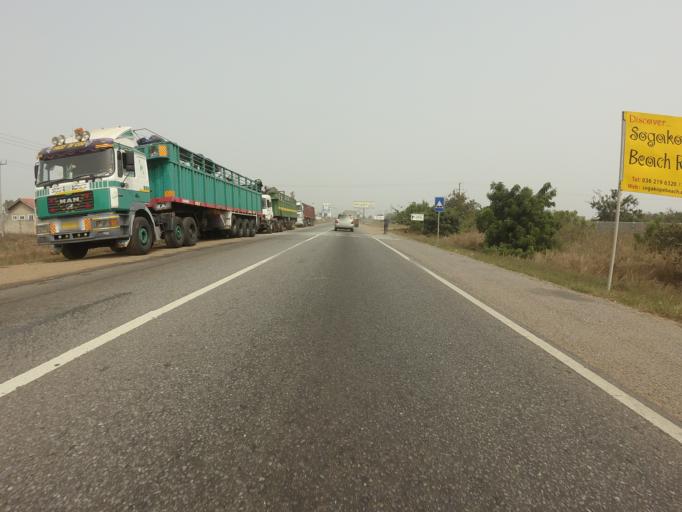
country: GH
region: Greater Accra
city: Tema
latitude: 5.7752
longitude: 0.0806
